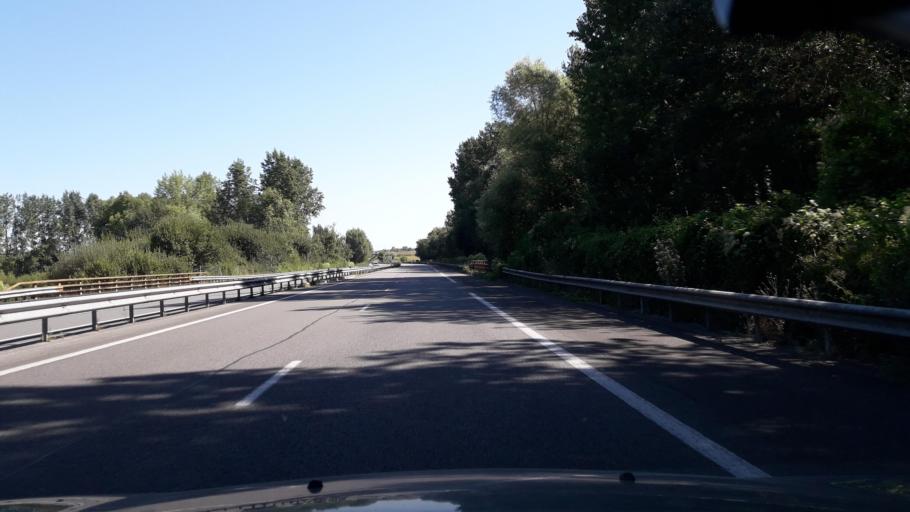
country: FR
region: Poitou-Charentes
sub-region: Departement de la Charente
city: Jarnac
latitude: 45.6805
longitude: -0.1463
